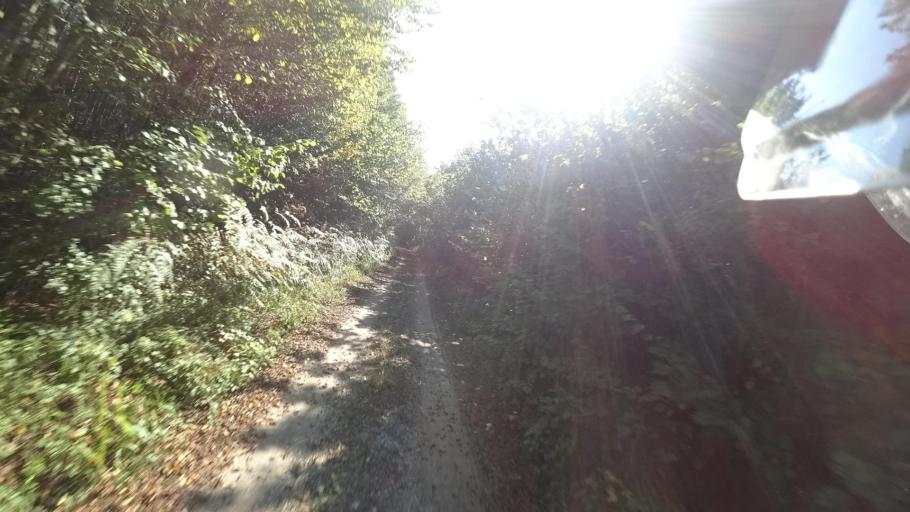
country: HR
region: Karlovacka
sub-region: Grad Ogulin
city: Ogulin
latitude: 45.2037
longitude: 15.1231
